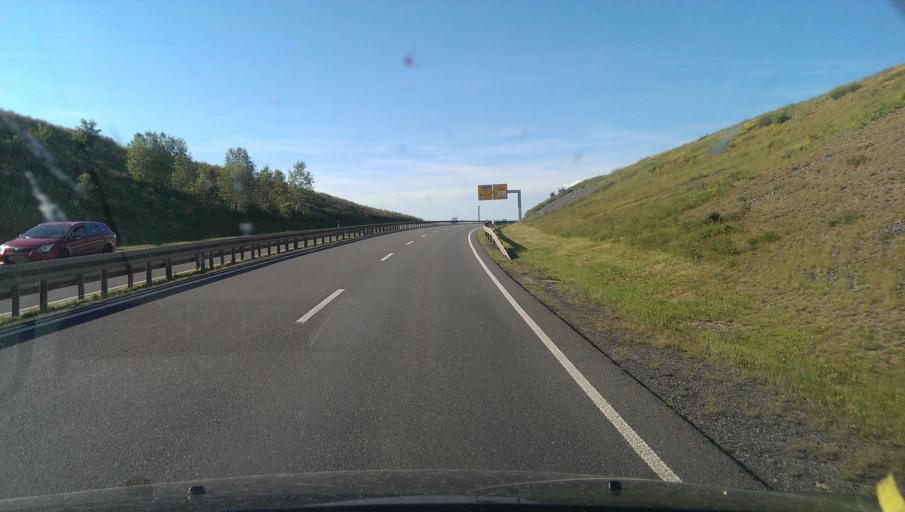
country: DE
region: Thuringia
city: Gera
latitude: 50.8894
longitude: 12.1122
